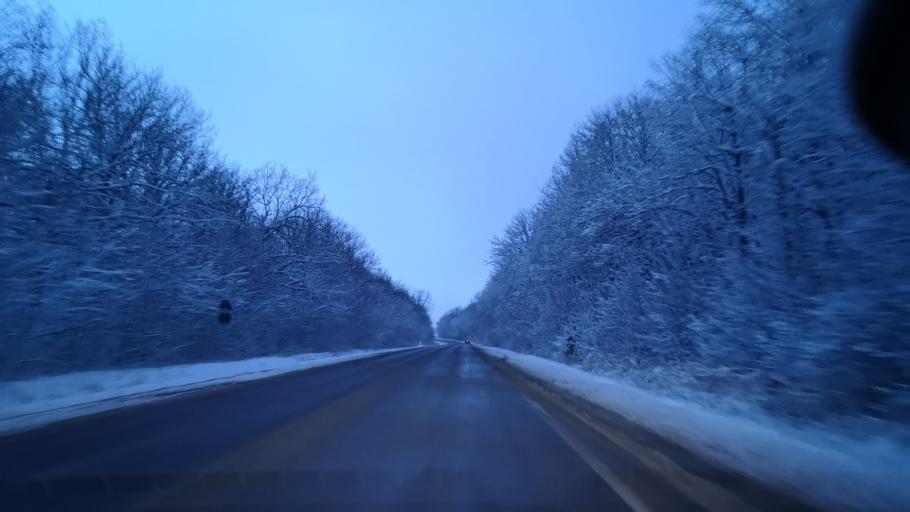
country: MD
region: Soldanesti
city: Soldanesti
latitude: 47.7237
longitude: 28.8555
